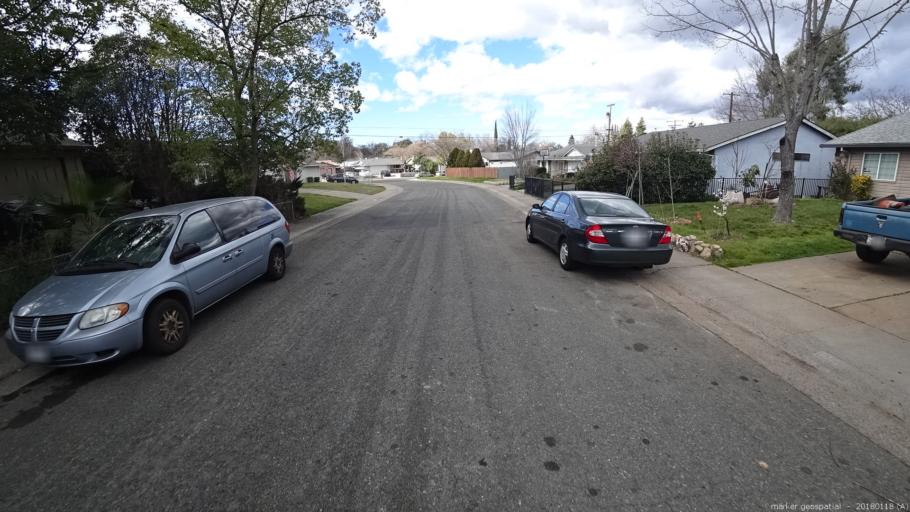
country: US
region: California
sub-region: Sacramento County
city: Orangevale
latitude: 38.6675
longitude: -121.2157
